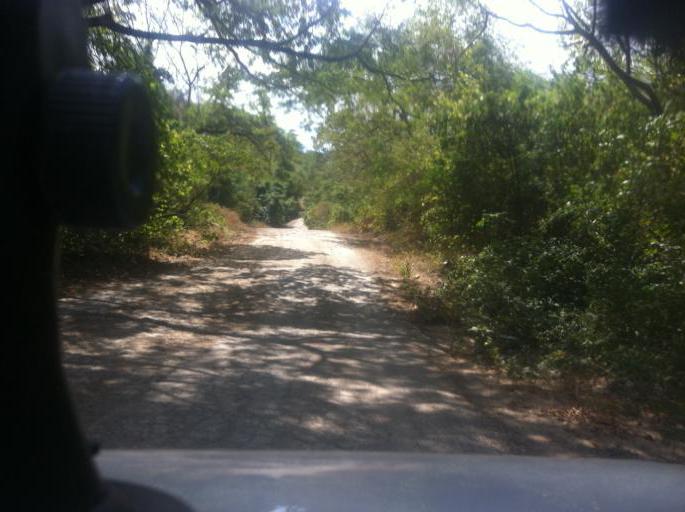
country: NI
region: Rivas
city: Belen
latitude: 11.5680
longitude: -86.0274
